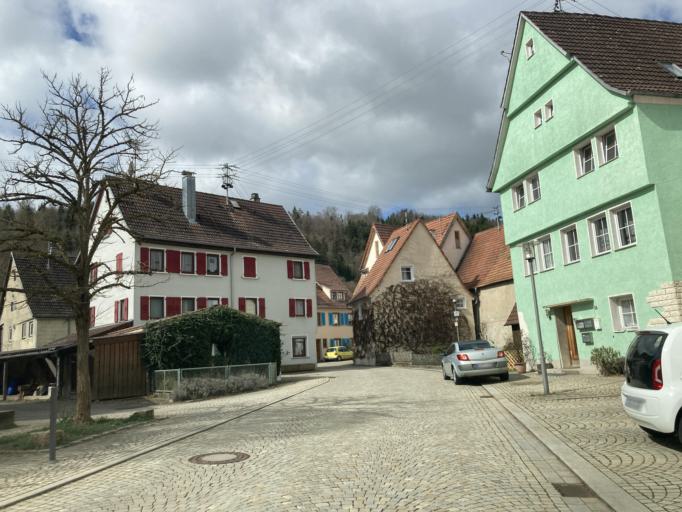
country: DE
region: Baden-Wuerttemberg
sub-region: Tuebingen Region
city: Hirrlingen
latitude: 48.4578
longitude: 8.8694
